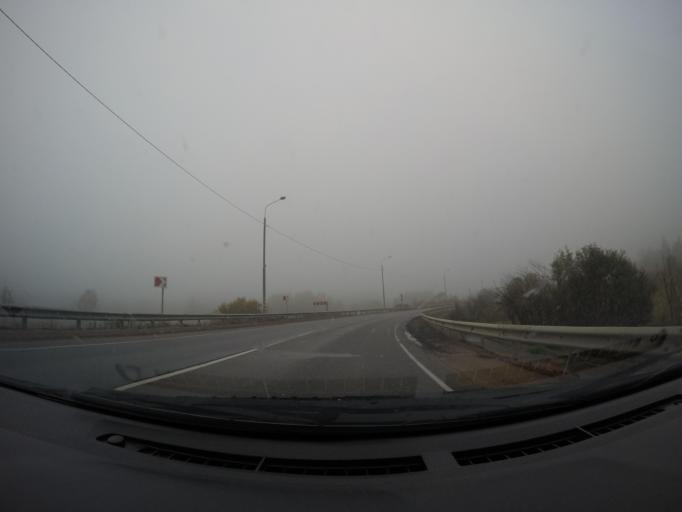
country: RU
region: Moskovskaya
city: Ruza
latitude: 55.7287
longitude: 36.3092
